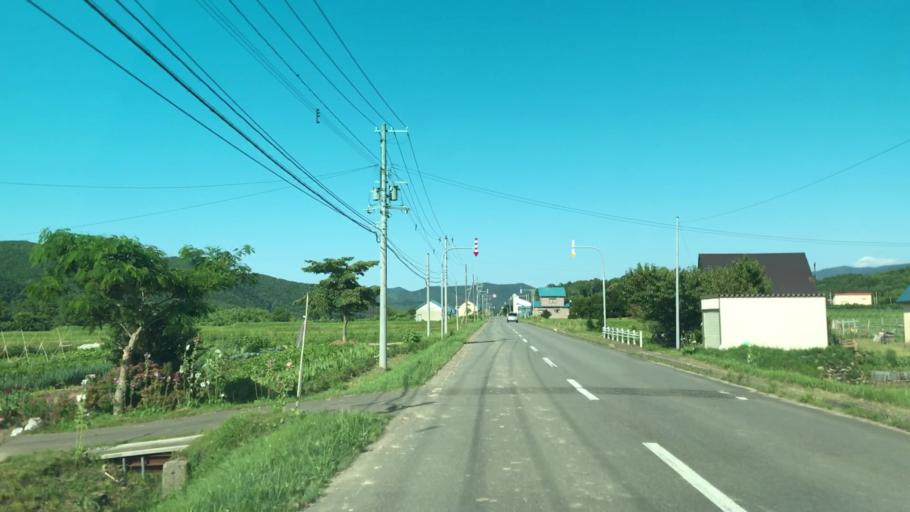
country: JP
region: Hokkaido
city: Yoichi
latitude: 43.0362
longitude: 140.7826
